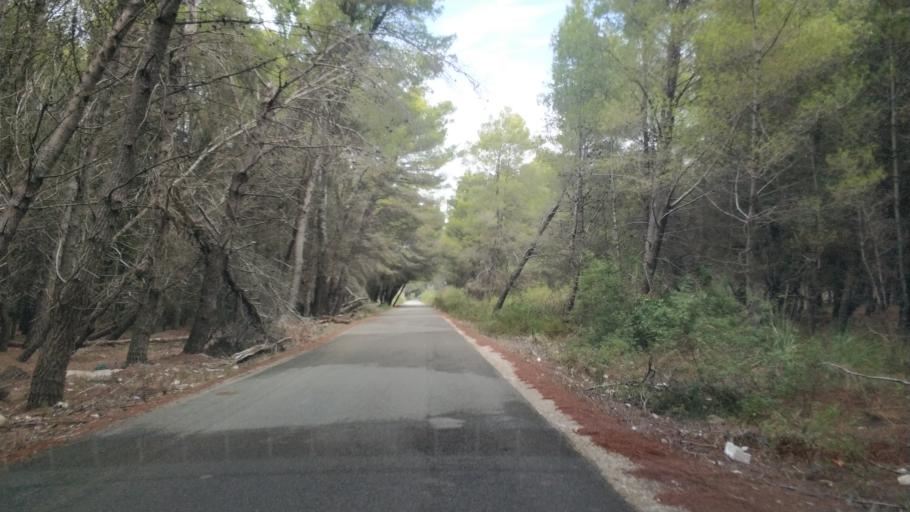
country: AL
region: Vlore
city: Vlore
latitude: 40.4928
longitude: 19.4357
